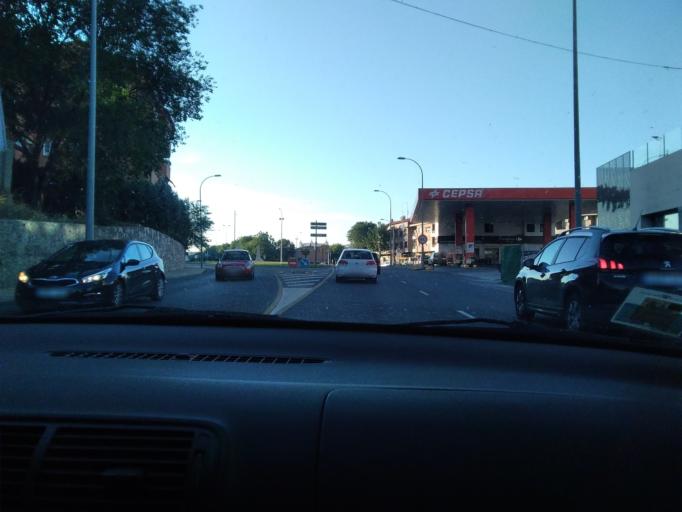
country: ES
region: Castille-La Mancha
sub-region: Province of Toledo
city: Toledo
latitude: 39.8731
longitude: -4.0406
